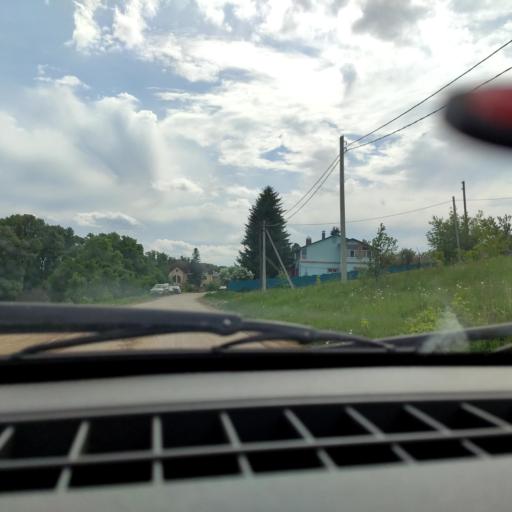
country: RU
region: Bashkortostan
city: Mikhaylovka
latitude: 54.8102
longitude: 55.8988
